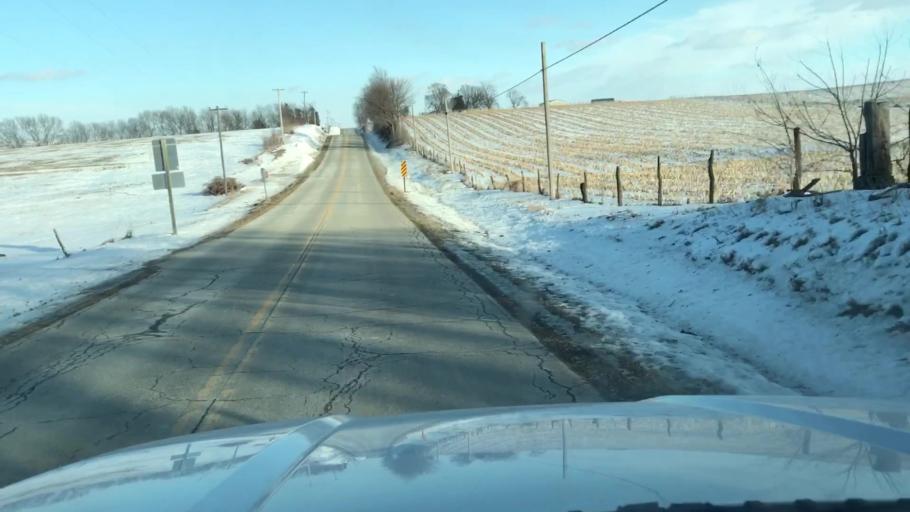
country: US
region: Missouri
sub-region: Andrew County
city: Savannah
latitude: 40.0251
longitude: -94.9681
